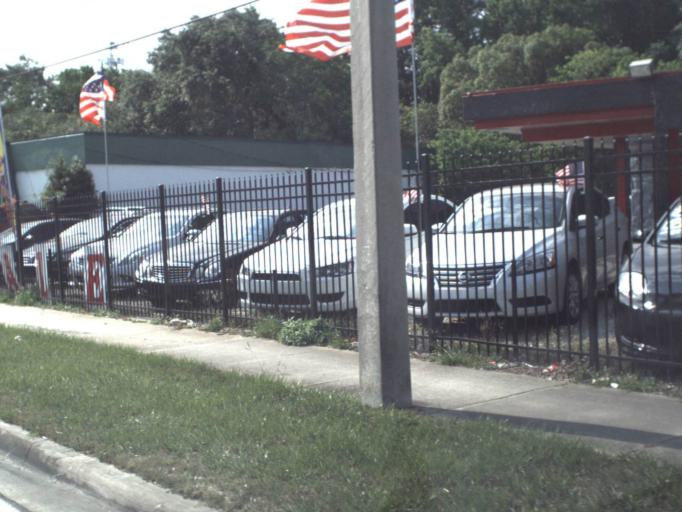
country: US
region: Florida
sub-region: Duval County
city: Jacksonville
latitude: 30.2940
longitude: -81.6067
